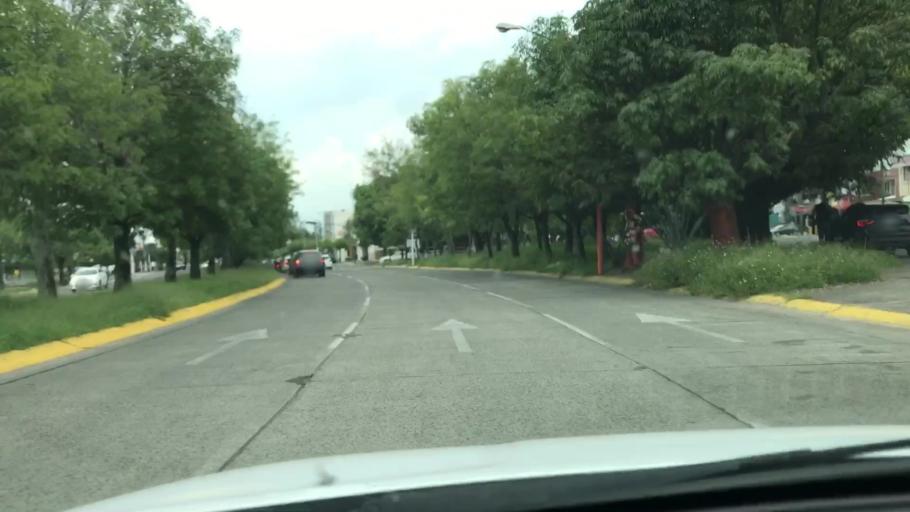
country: MX
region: Jalisco
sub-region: Tlajomulco de Zuniga
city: Palomar
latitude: 20.6352
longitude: -103.4328
